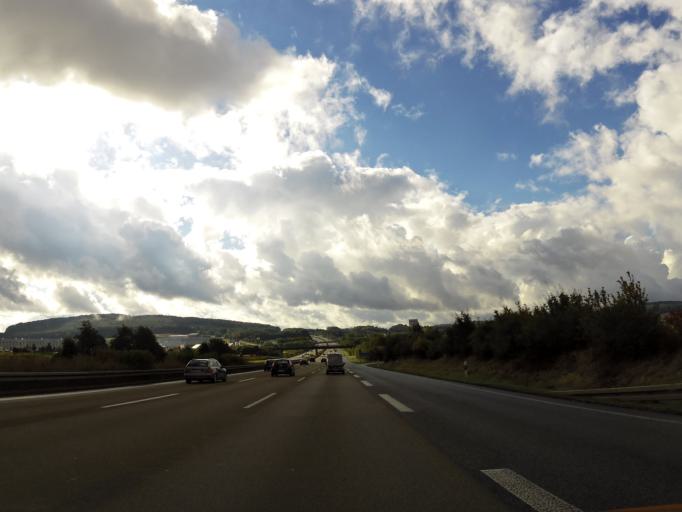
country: DE
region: Hesse
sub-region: Regierungsbezirk Kassel
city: Malsfeld
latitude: 51.0912
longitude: 9.4835
